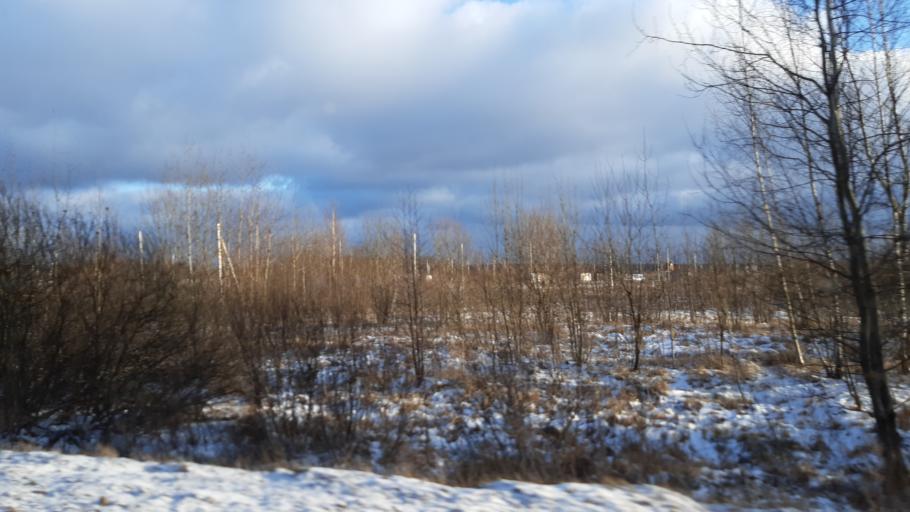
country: RU
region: Moskovskaya
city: Noginsk-9
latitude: 56.0595
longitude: 38.5523
